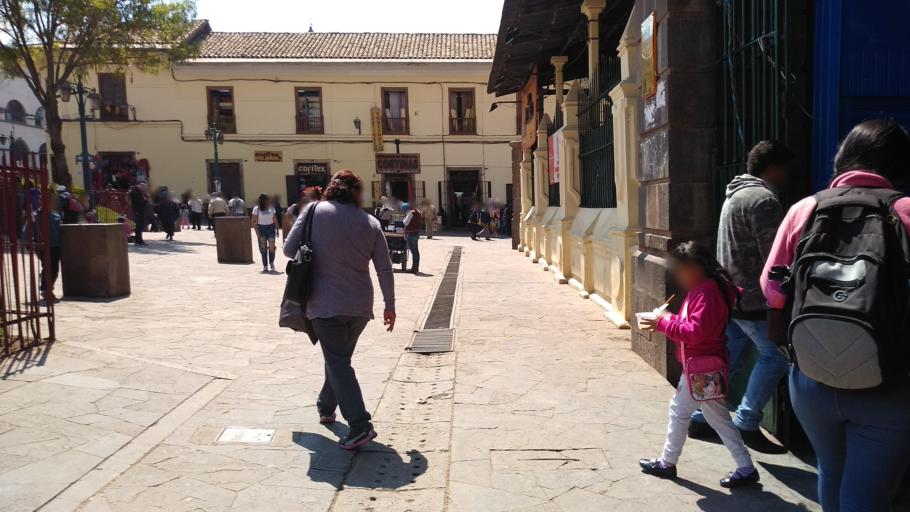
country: PE
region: Cusco
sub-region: Provincia de Cusco
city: Cusco
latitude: -13.5206
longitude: -71.9829
